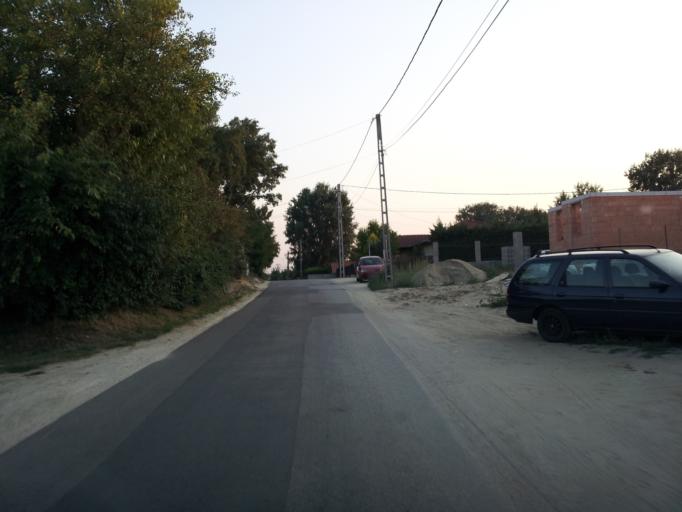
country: HU
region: Pest
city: Szigethalom
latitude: 47.3214
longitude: 19.0238
